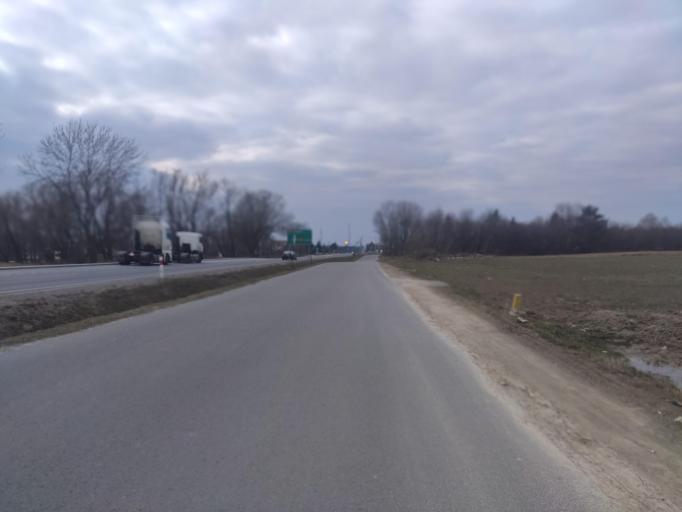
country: PL
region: Lublin Voivodeship
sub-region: Powiat lubartowski
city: Kock
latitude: 51.6449
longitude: 22.4411
